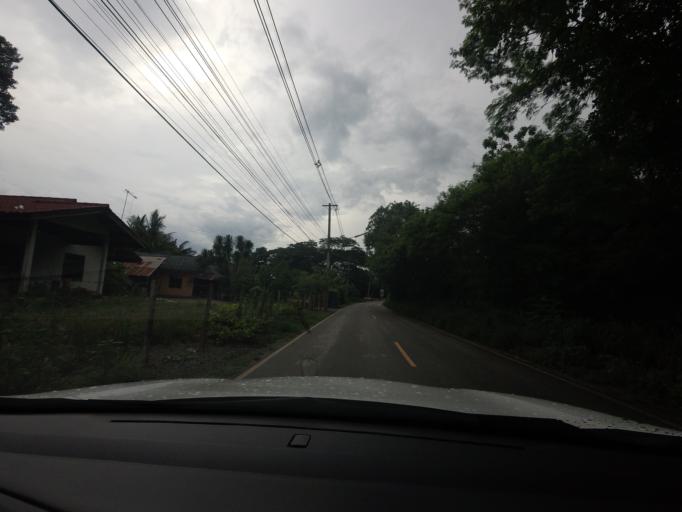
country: TH
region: Nakhon Ratchasima
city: Pak Chong
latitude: 14.6213
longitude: 101.4404
